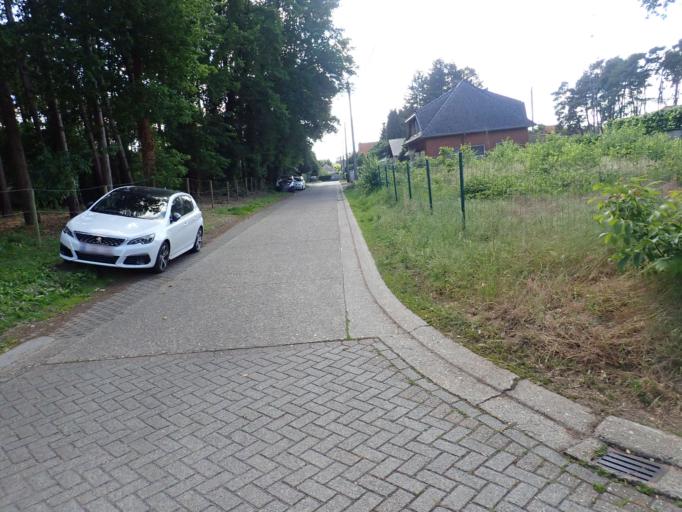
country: BE
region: Flanders
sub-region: Provincie Antwerpen
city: Kasterlee
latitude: 51.2206
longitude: 4.9240
